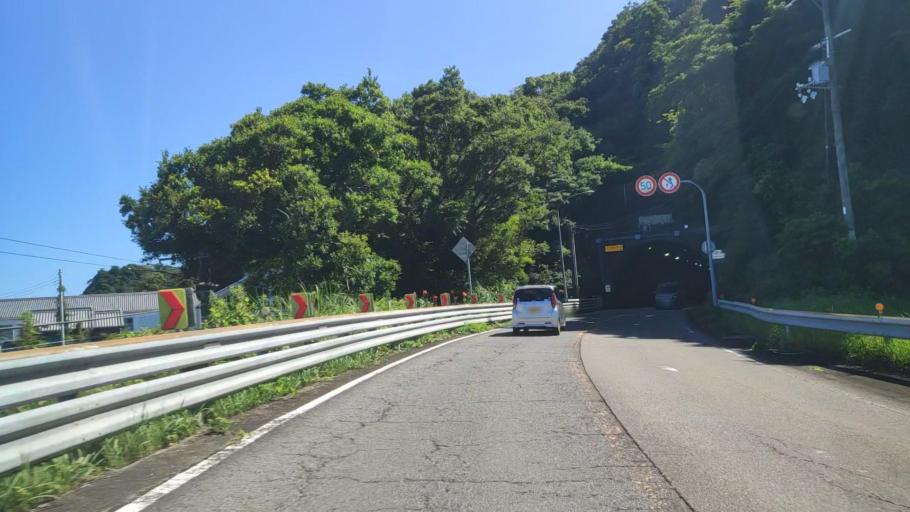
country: JP
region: Wakayama
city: Shingu
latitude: 33.5764
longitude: 135.9188
